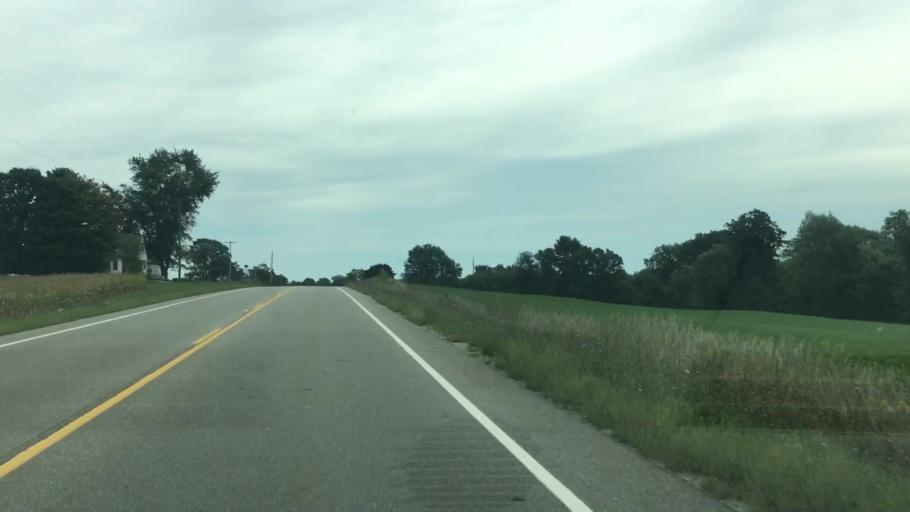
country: US
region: Michigan
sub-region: Kent County
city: Byron Center
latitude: 42.8116
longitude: -85.7964
